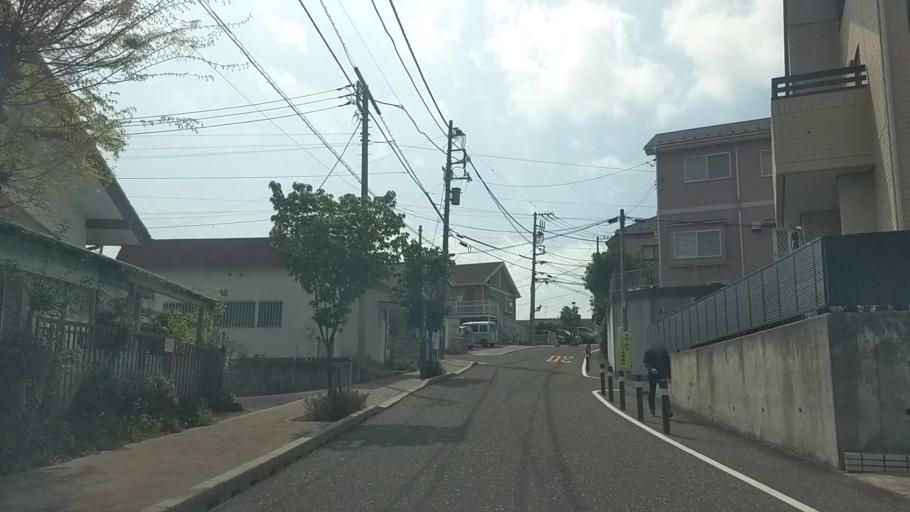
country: JP
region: Kanagawa
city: Yokohama
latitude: 35.3960
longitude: 139.5920
